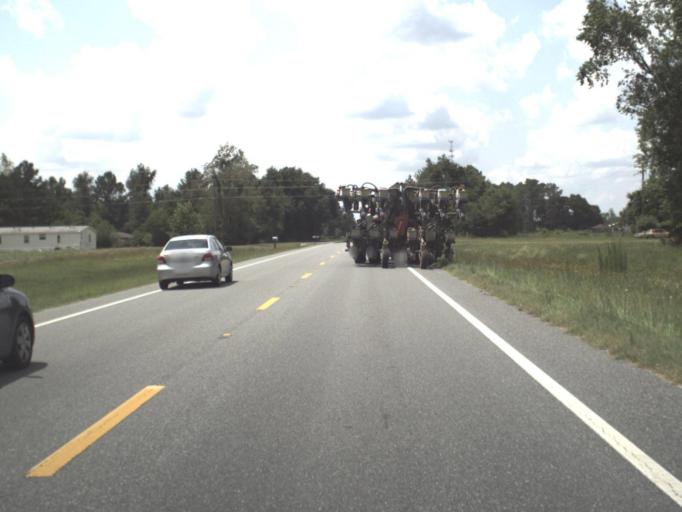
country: US
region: Florida
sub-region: Hamilton County
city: Jasper
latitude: 30.5398
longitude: -83.0505
